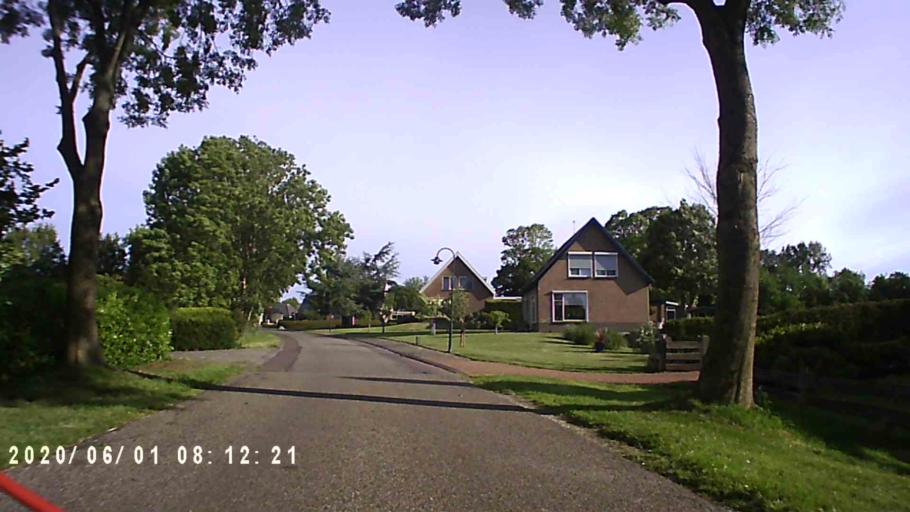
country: NL
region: Friesland
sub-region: Gemeente Ferwerderadiel
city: Burdaard
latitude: 53.2924
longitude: 5.8813
